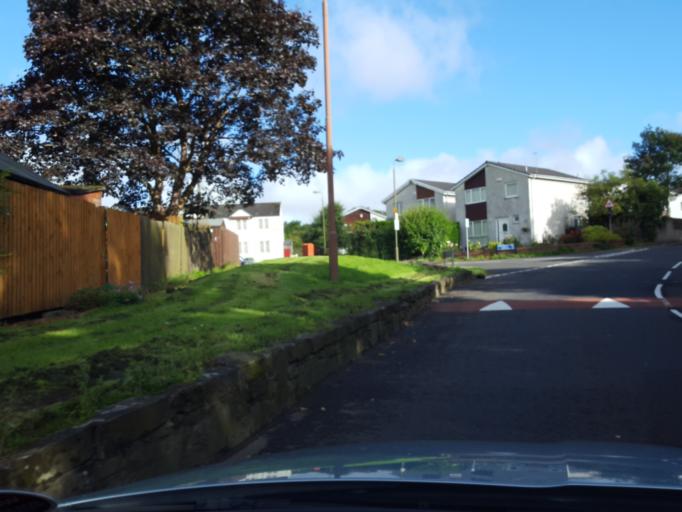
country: GB
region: Scotland
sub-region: West Lothian
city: Livingston
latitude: 55.9314
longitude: -3.5081
